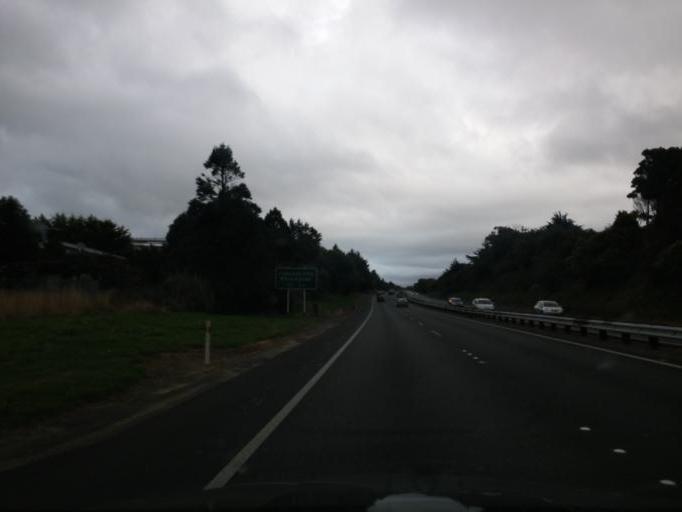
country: NZ
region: Wellington
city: Petone
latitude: -41.2099
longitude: 174.8160
